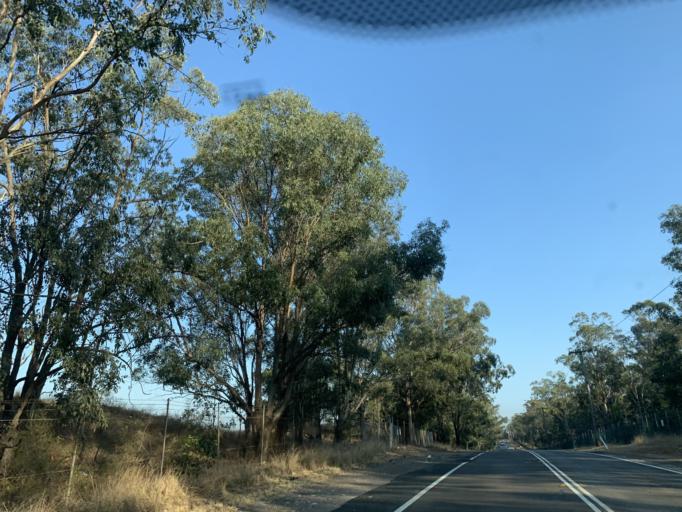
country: AU
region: New South Wales
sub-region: Fairfield
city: Horsley Park
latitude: -33.8294
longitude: 150.8728
